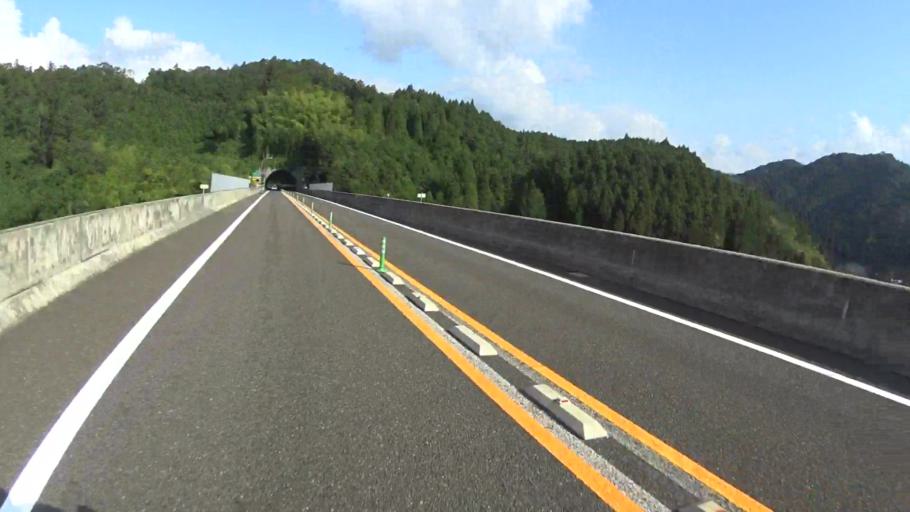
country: JP
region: Kyoto
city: Ayabe
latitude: 35.4070
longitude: 135.2278
